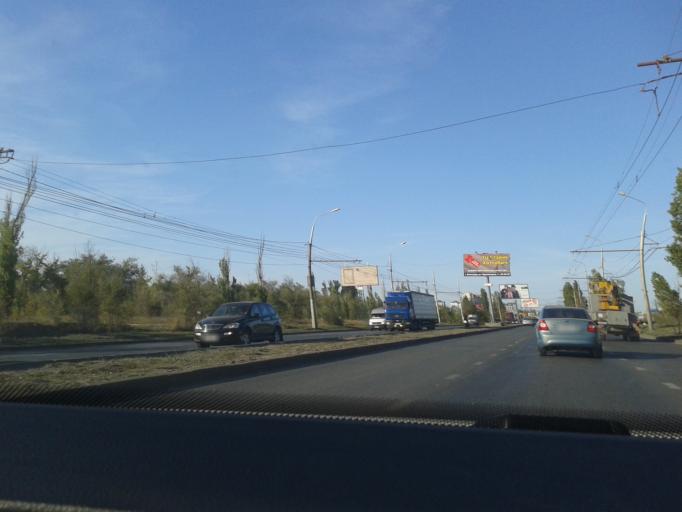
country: RU
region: Volgograd
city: Volgograd
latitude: 48.6304
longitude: 44.4281
